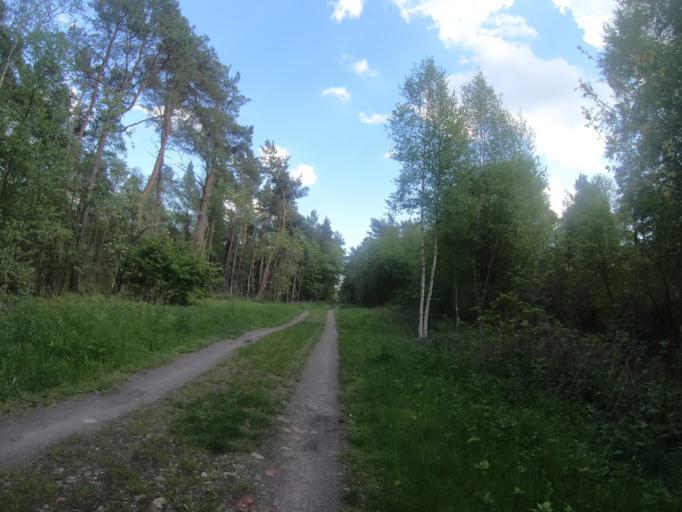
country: DE
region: Lower Saxony
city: Sassenburg
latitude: 52.5258
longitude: 10.6189
